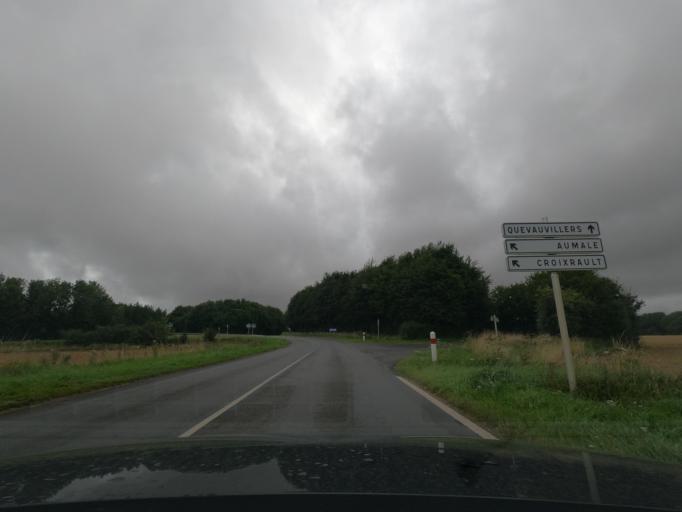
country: FR
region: Picardie
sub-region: Departement de la Somme
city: Poix-de-Picardie
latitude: 49.7826
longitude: 2.0019
